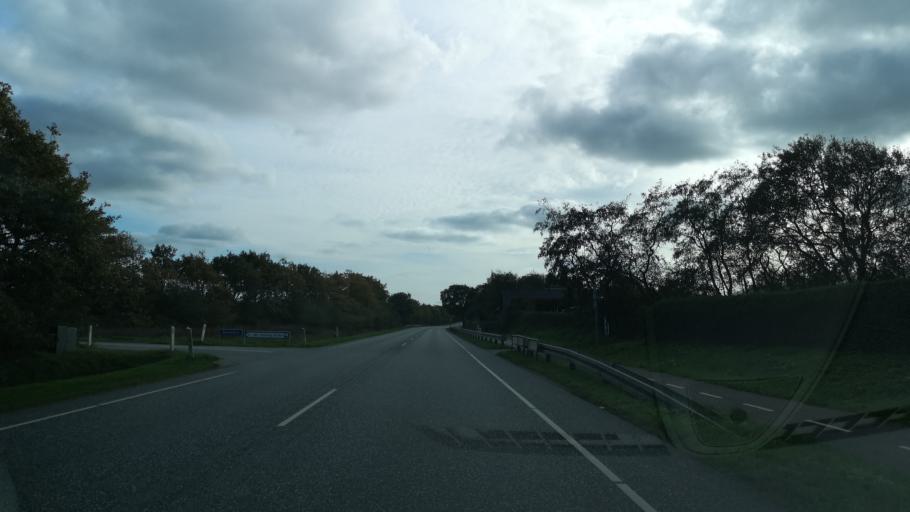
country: DK
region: Central Jutland
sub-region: Holstebro Kommune
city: Holstebro
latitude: 56.3301
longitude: 8.6107
